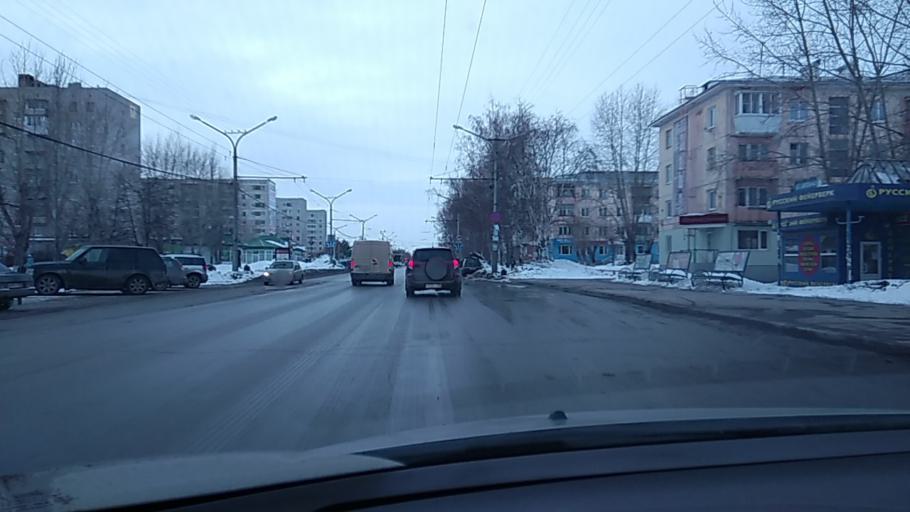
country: RU
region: Sverdlovsk
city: Martyush
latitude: 56.4262
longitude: 61.8943
